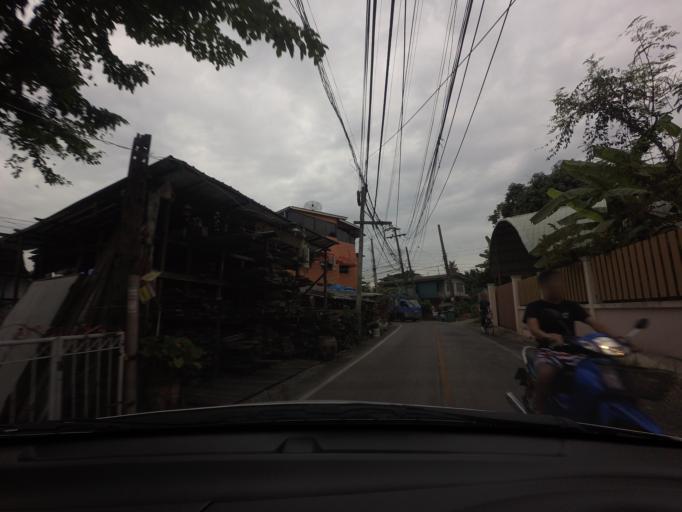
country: TH
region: Bangkok
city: Yan Nawa
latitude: 13.6948
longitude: 100.5607
